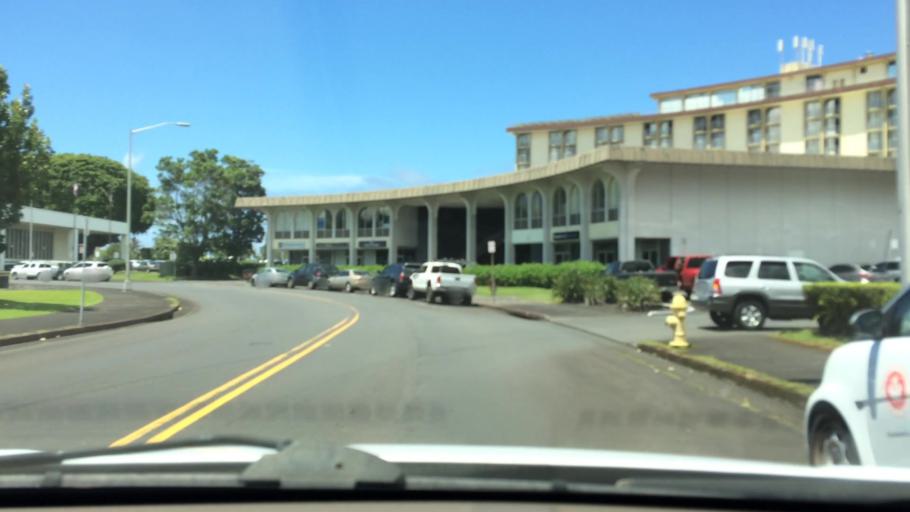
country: US
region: Hawaii
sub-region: Hawaii County
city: Hilo
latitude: 19.7172
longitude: -155.0776
